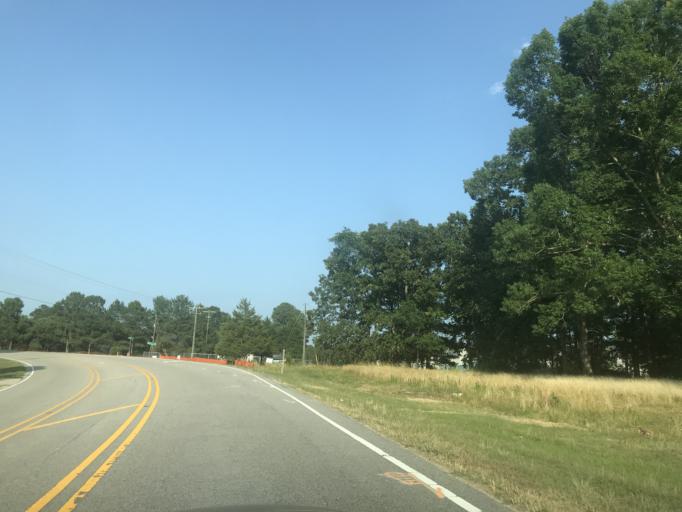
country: US
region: North Carolina
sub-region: Wake County
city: Knightdale
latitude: 35.8283
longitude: -78.5049
